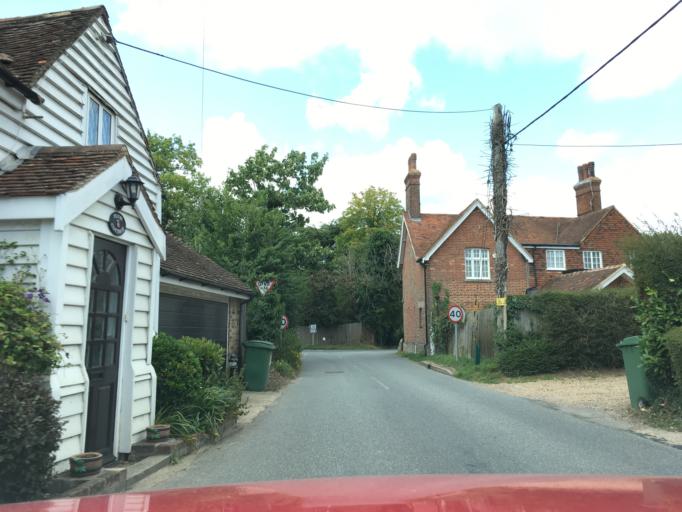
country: GB
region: England
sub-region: Kent
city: Staplehurst
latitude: 51.2242
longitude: 0.5715
